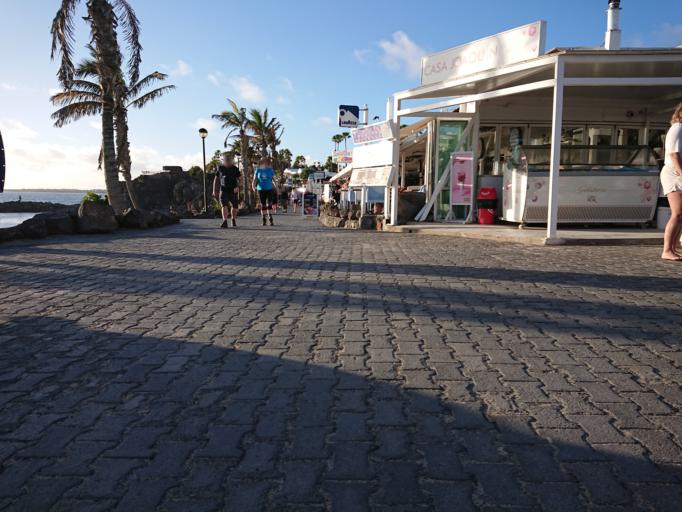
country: ES
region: Canary Islands
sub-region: Provincia de Las Palmas
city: Playa Blanca
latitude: 28.8580
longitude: -13.8417
